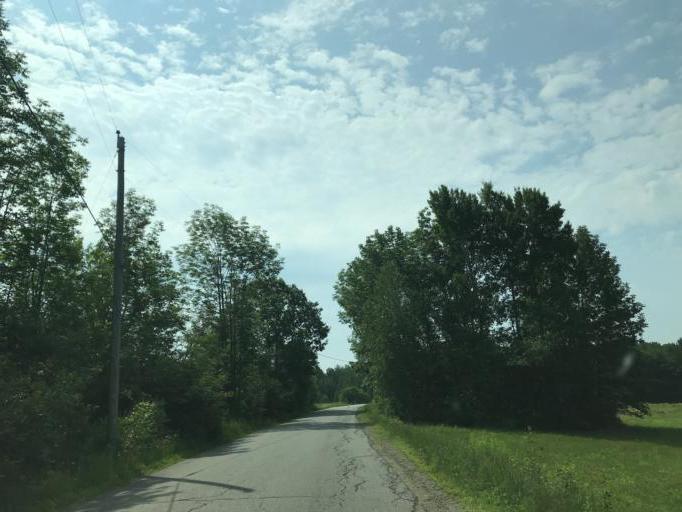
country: US
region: Maine
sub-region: Knox County
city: Hope
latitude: 44.2202
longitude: -69.1727
